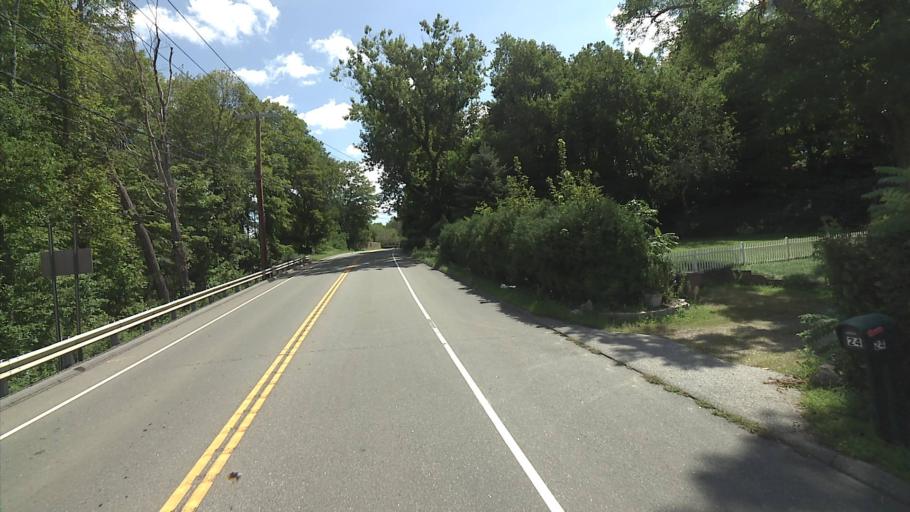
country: US
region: Connecticut
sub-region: New London County
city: Niantic
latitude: 41.3698
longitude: -72.1960
